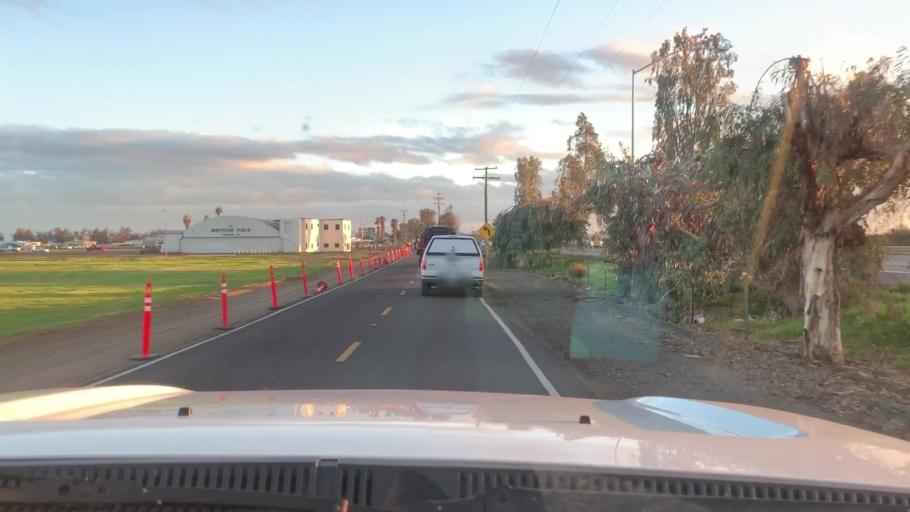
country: US
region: California
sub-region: Tulare County
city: Tulare
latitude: 36.1558
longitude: -119.3319
